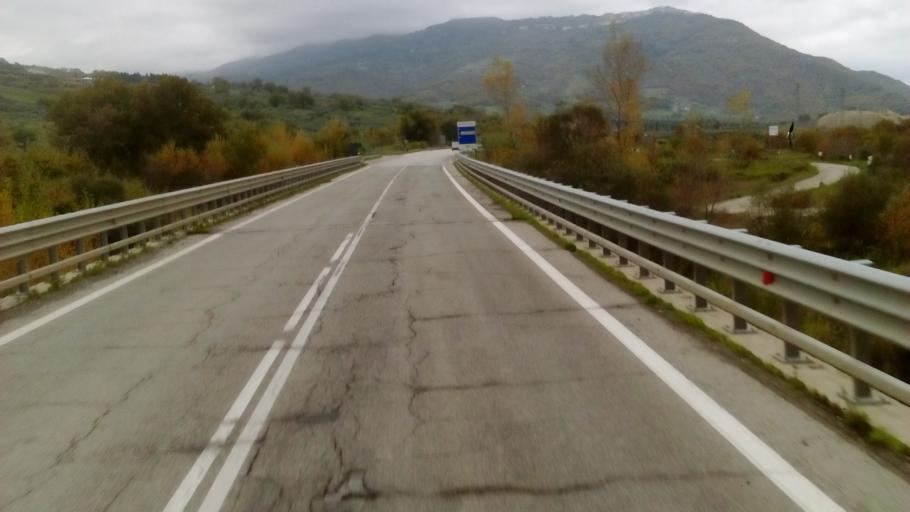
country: IT
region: Abruzzo
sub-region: Provincia di Chieti
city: Celenza sul Trigno
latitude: 41.8679
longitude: 14.6046
